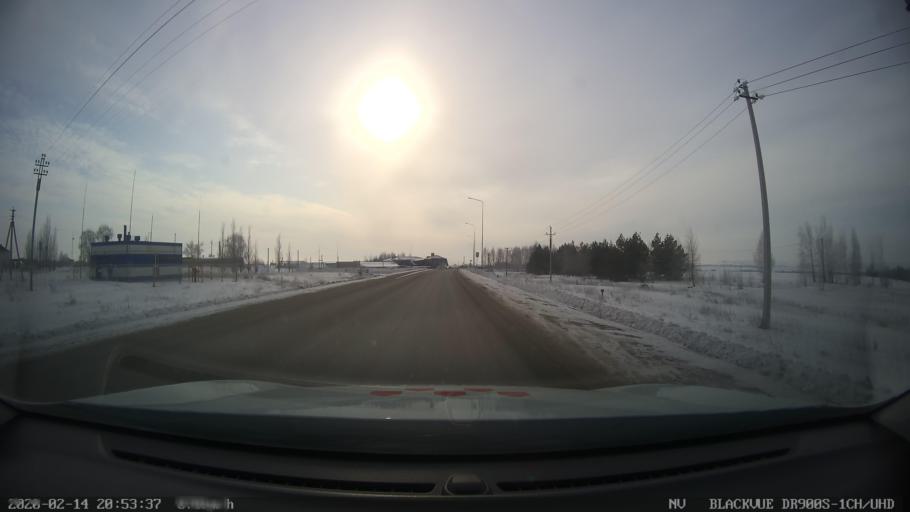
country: RU
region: Tatarstan
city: Kuybyshevskiy Zaton
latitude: 55.1925
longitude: 49.2474
